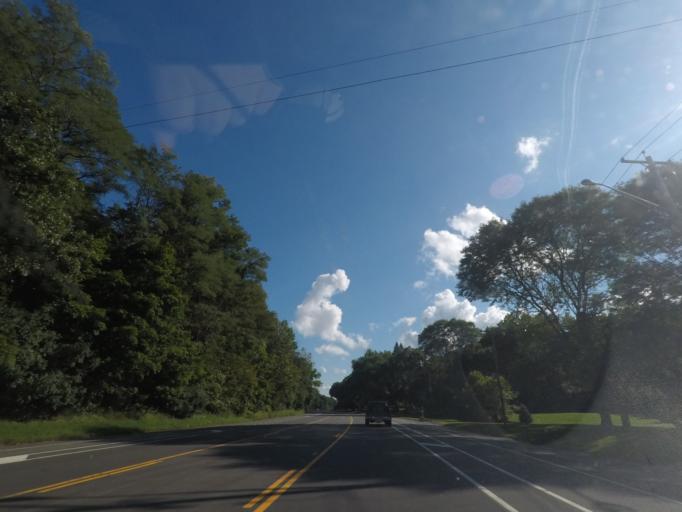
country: US
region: New York
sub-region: Albany County
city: Menands
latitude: 42.6947
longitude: -73.7402
